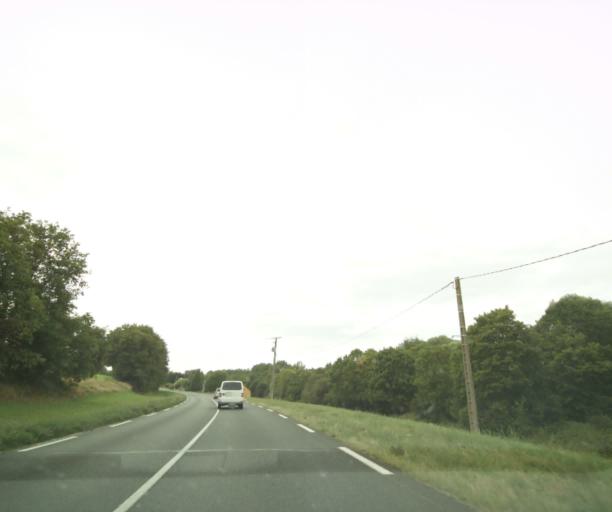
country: FR
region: Centre
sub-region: Departement d'Indre-et-Loire
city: Perrusson
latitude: 47.0695
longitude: 1.0773
